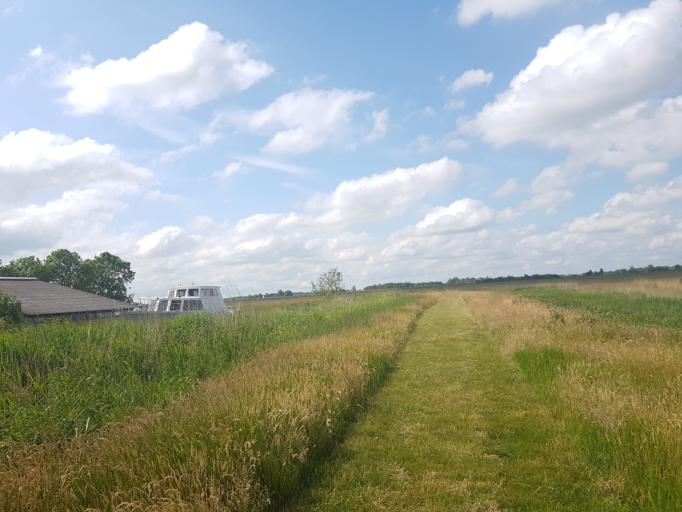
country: NL
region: Friesland
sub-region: Gemeente Boarnsterhim
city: Aldeboarn
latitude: 53.0934
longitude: 5.9153
